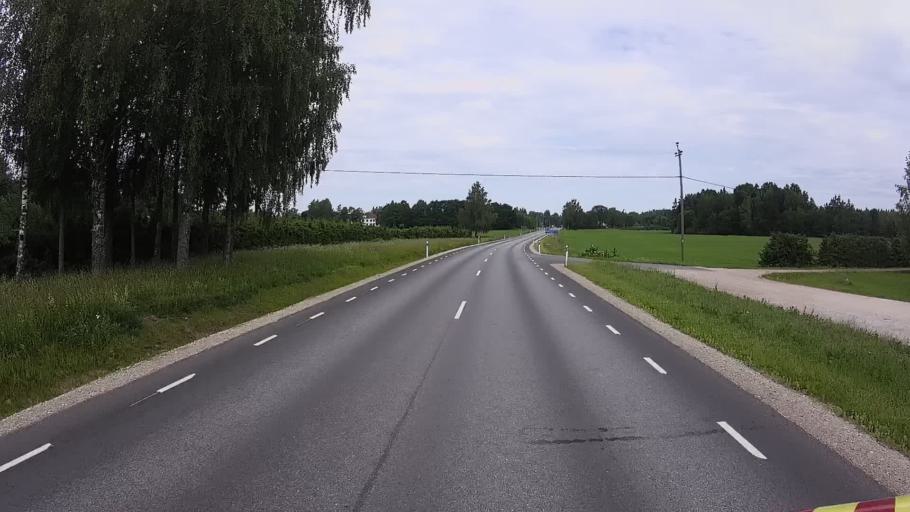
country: EE
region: Viljandimaa
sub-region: Viljandi linn
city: Viljandi
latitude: 58.2365
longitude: 25.5976
